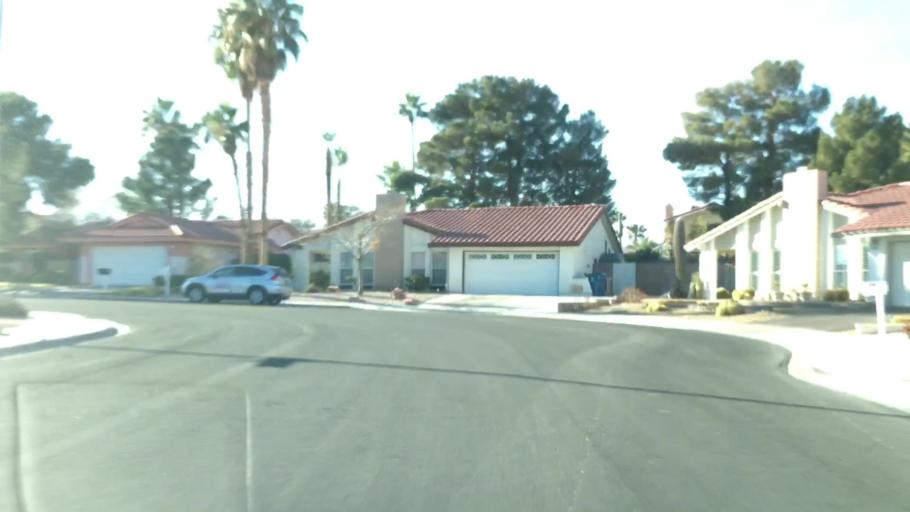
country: US
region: Nevada
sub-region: Clark County
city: Summerlin South
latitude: 36.1562
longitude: -115.2854
